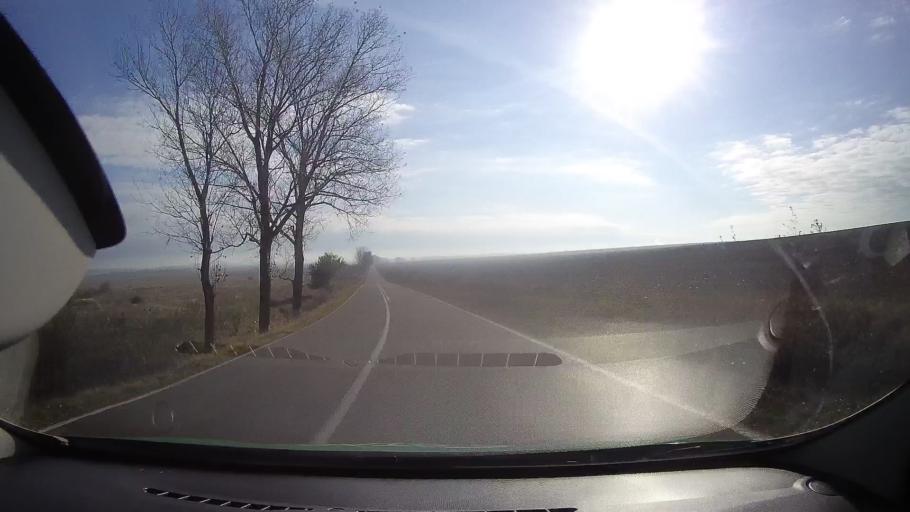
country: RO
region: Tulcea
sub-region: Comuna Mahmudia
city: Mahmudia
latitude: 45.0723
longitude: 29.0935
